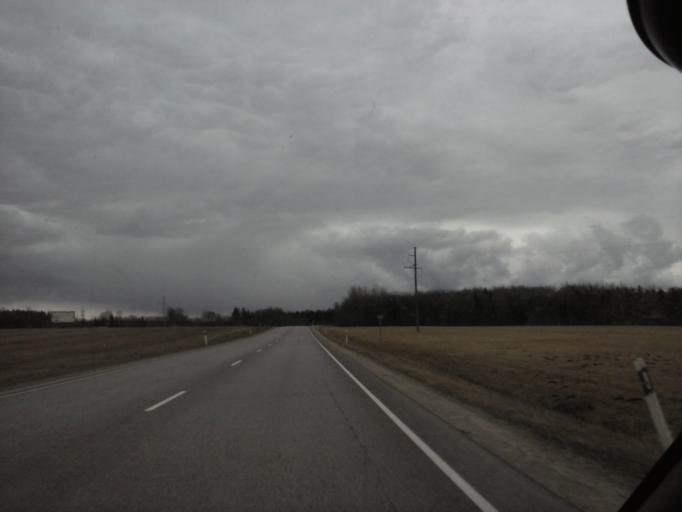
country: EE
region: Jaervamaa
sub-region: Paide linn
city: Paide
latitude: 58.8236
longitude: 25.7502
